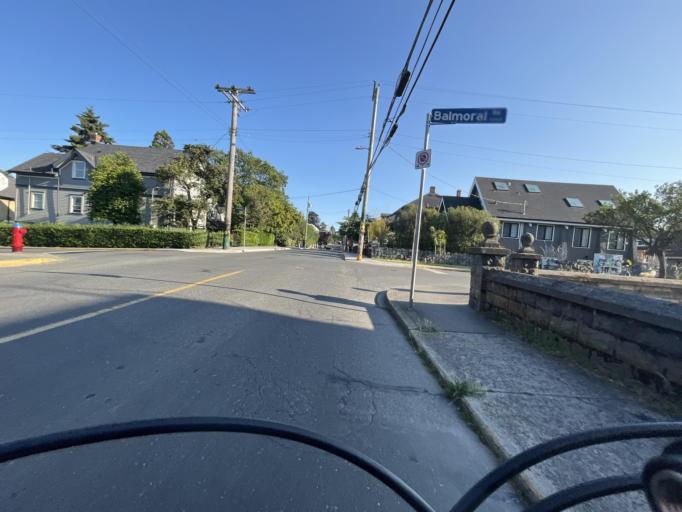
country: CA
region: British Columbia
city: Victoria
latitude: 48.4279
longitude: -123.3454
